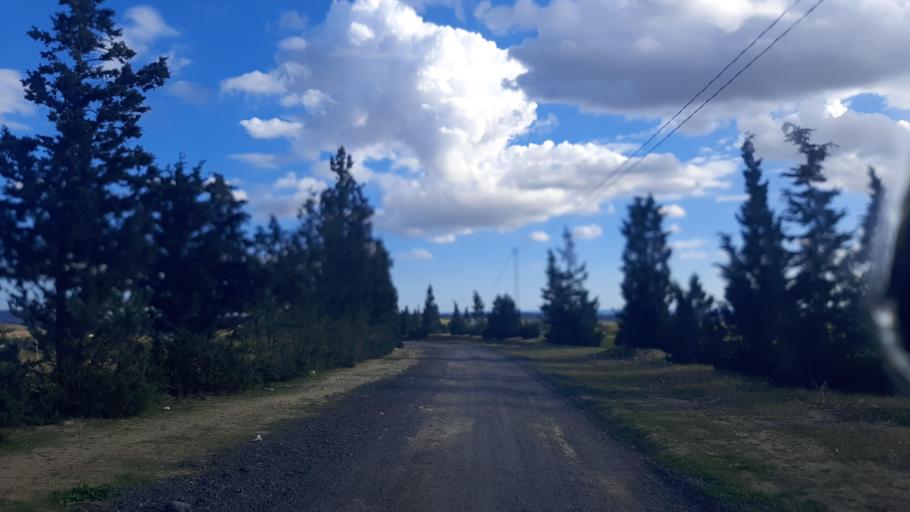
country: TN
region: Nabul
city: Bu `Urqub
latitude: 36.4698
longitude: 10.4769
